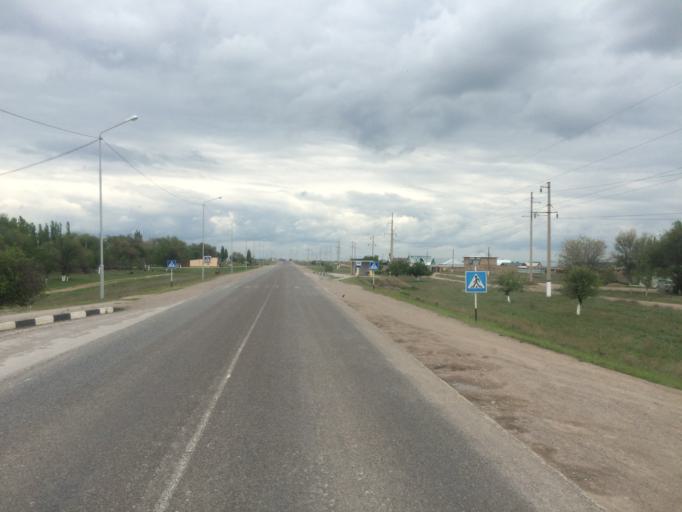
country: KG
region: Chuy
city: Sokuluk
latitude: 43.2491
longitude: 74.2919
